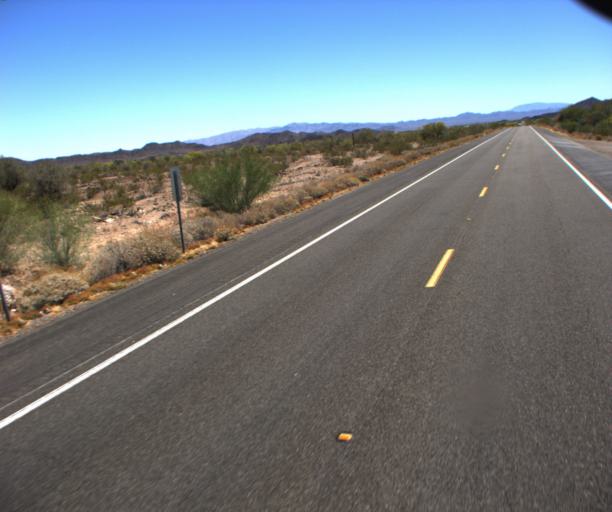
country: US
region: Arizona
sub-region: La Paz County
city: Quartzsite
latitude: 33.6702
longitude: -113.9835
